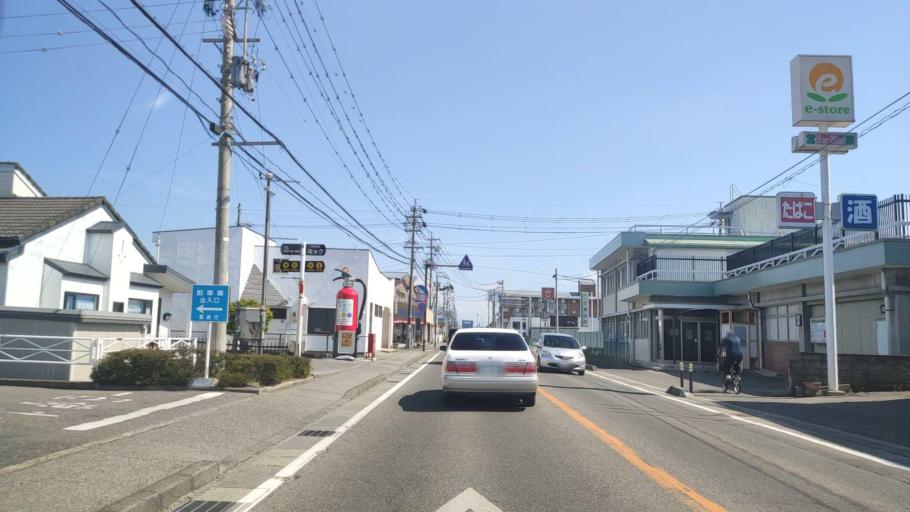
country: JP
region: Nagano
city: Hotaka
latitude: 36.3377
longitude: 137.8889
